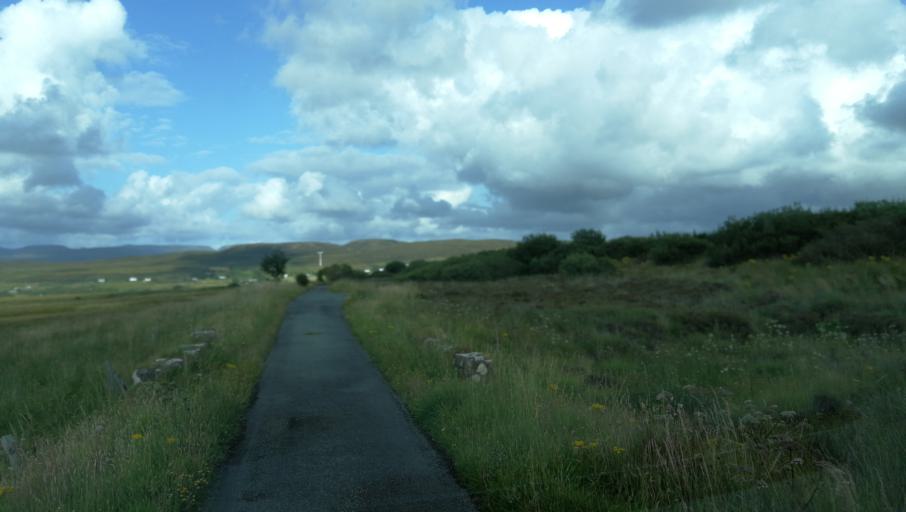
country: GB
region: Scotland
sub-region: Highland
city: Isle of Skye
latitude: 57.4722
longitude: -6.4587
